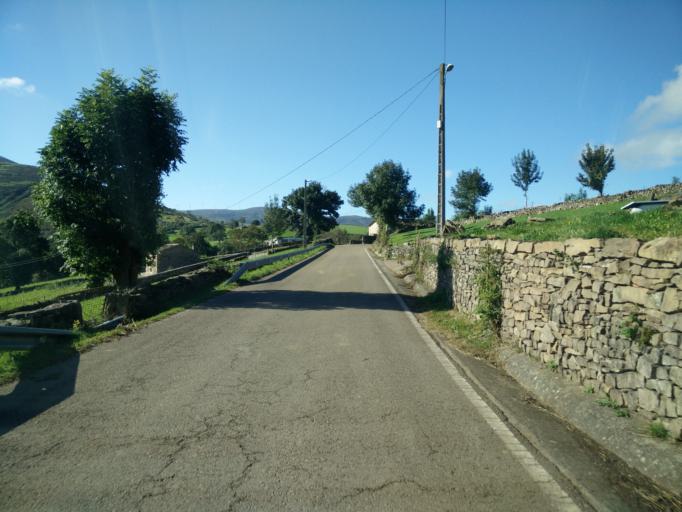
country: ES
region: Cantabria
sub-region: Provincia de Cantabria
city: San Pedro del Romeral
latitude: 43.1076
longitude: -3.8173
